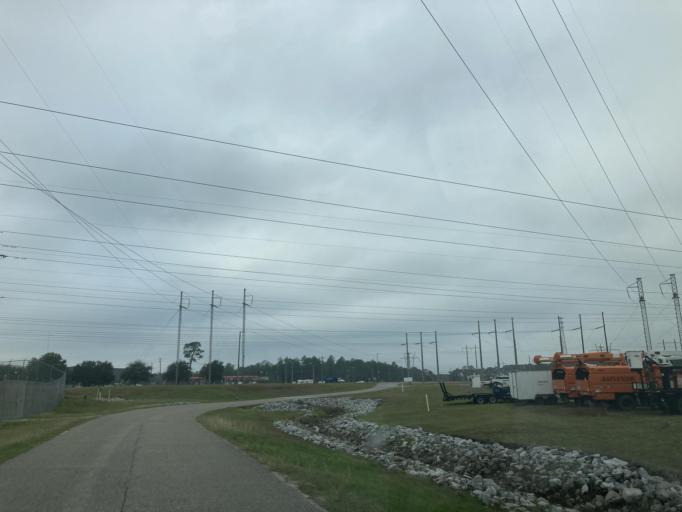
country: US
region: Mississippi
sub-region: Harrison County
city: West Gulfport
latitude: 30.4410
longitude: -89.0283
